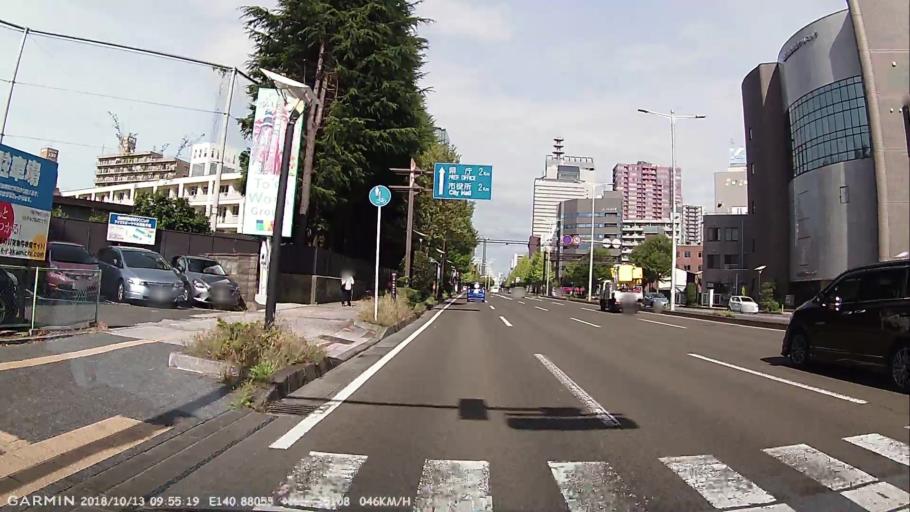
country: JP
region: Miyagi
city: Sendai
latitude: 38.2510
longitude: 140.8805
